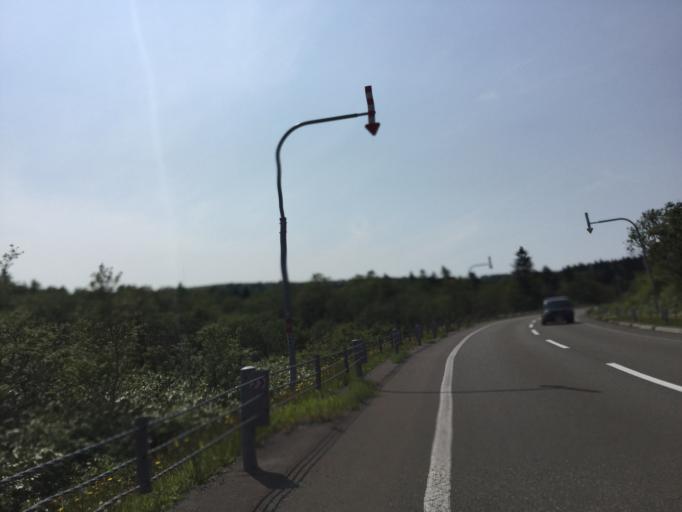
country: JP
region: Hokkaido
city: Makubetsu
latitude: 45.4064
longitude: 141.9649
